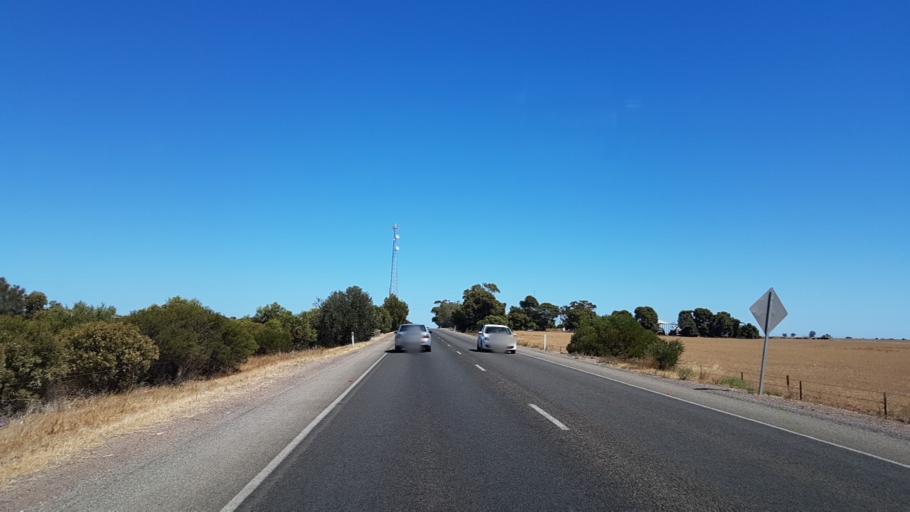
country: AU
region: South Australia
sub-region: Copper Coast
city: Wallaroo
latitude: -33.9498
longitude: 137.6742
